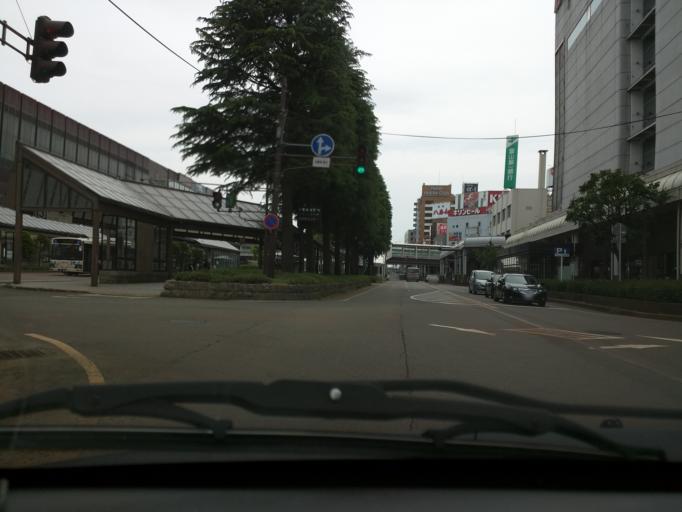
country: JP
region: Niigata
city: Nagaoka
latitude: 37.4484
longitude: 138.8532
